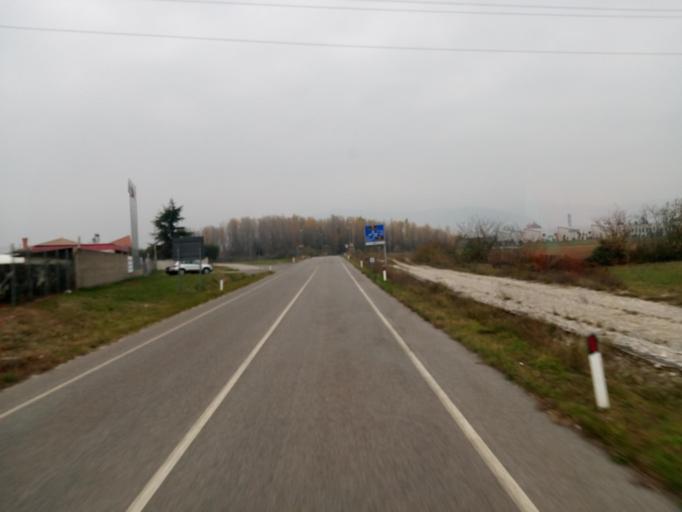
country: IT
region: Friuli Venezia Giulia
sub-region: Provincia di Udine
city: Moimacco
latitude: 46.0798
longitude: 13.3851
